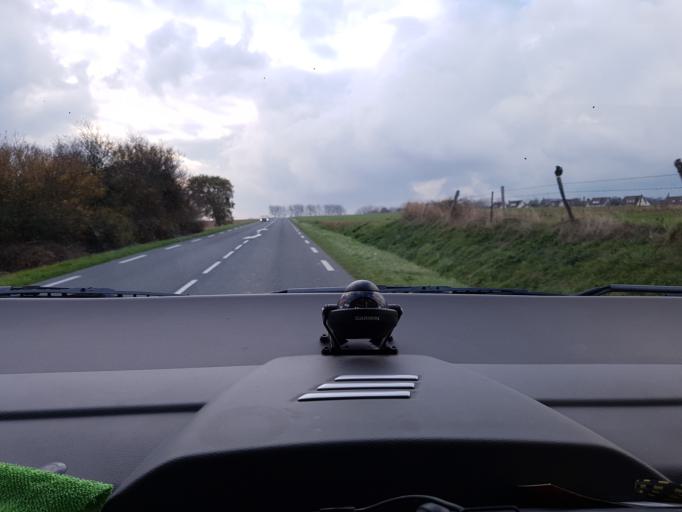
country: FR
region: Haute-Normandie
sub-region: Departement de la Seine-Maritime
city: Hautot-sur-Mer
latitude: 49.8932
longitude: 1.0463
